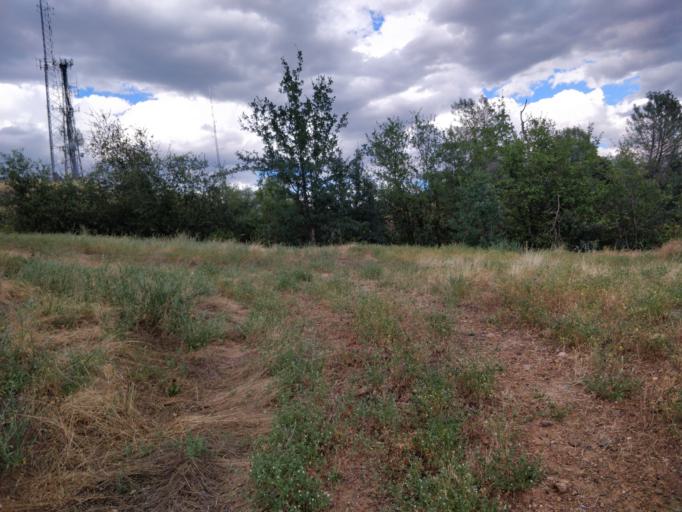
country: US
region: California
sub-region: Shasta County
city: Redding
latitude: 40.6099
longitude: -122.3832
